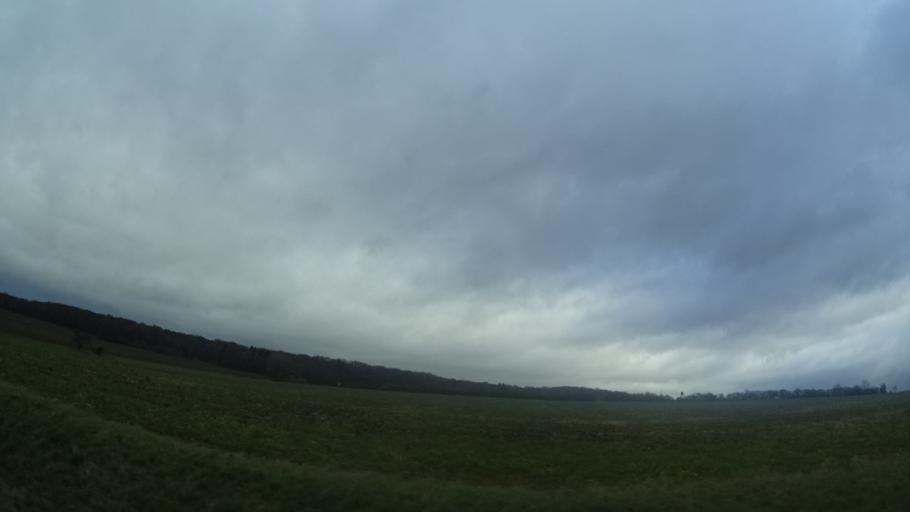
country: DE
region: Thuringia
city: Nauendorf
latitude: 50.9182
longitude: 11.1748
